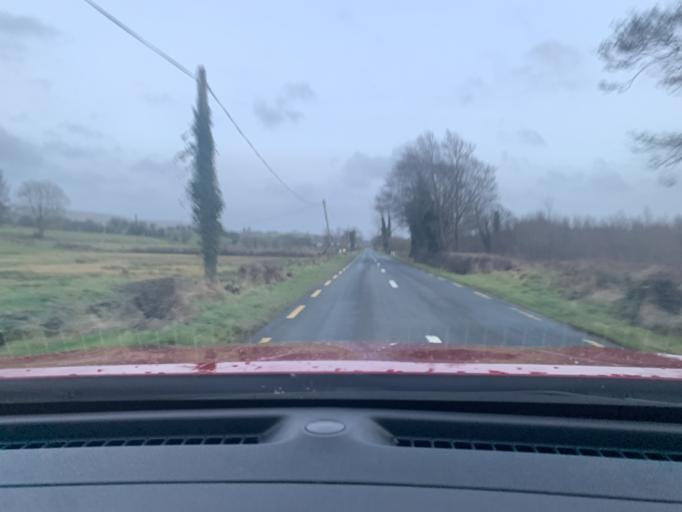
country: IE
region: Connaught
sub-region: Sligo
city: Ballymote
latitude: 54.0423
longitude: -8.4395
